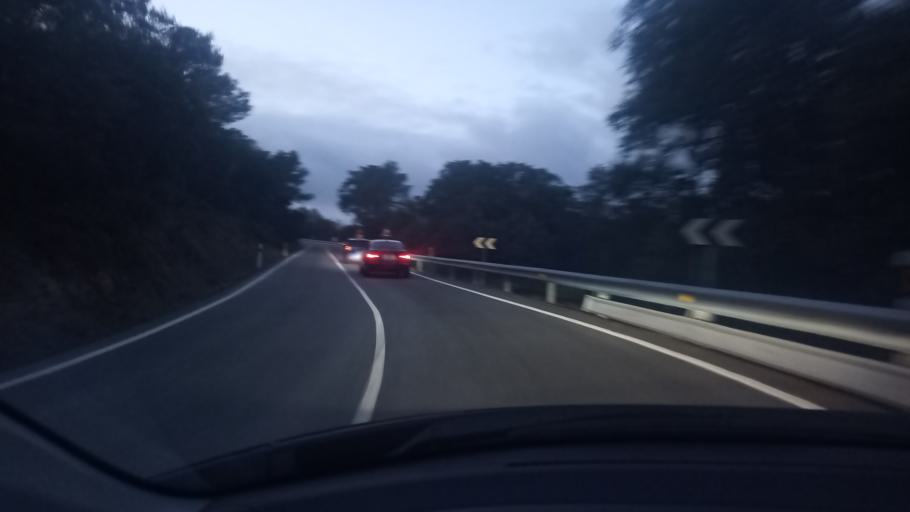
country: ES
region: Madrid
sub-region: Provincia de Madrid
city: Robledo de Chavela
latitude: 40.4611
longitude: -4.2614
